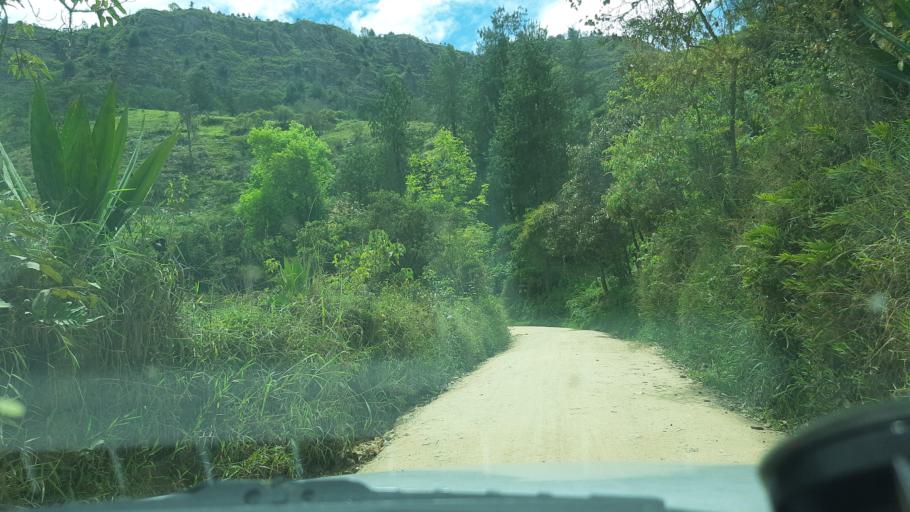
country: CO
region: Cundinamarca
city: Umbita
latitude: 5.2199
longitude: -73.4344
